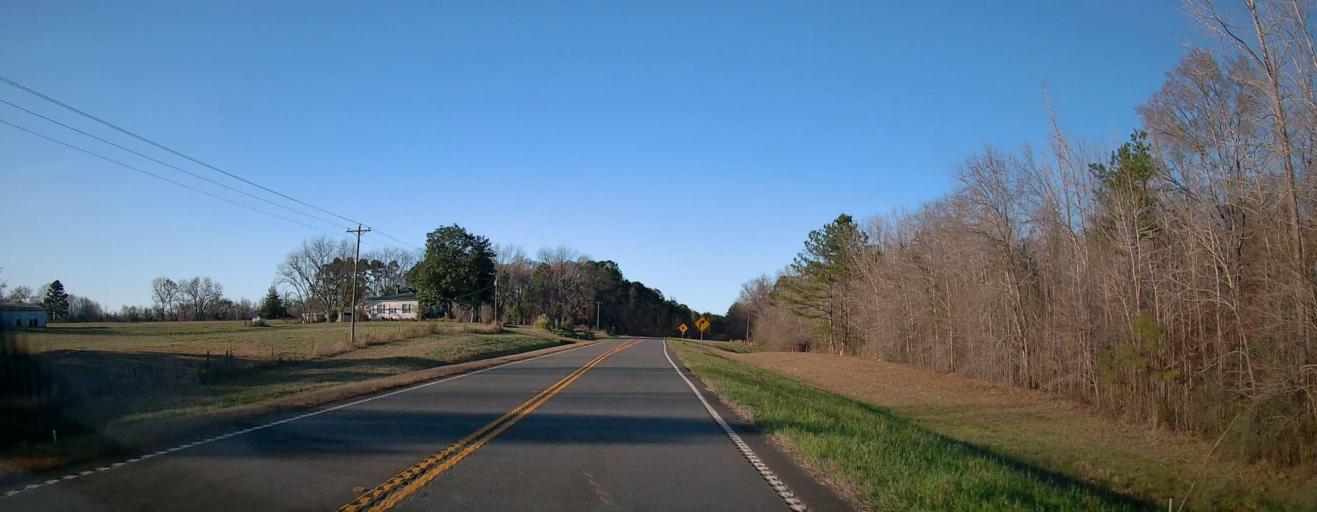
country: US
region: Georgia
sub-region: Talbot County
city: Talbotton
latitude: 32.5976
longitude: -84.5563
